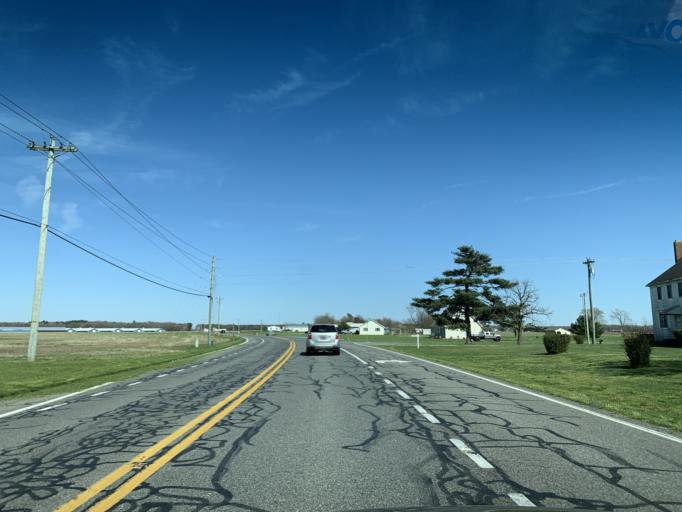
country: US
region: Delaware
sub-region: Kent County
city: Harrington
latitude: 38.8940
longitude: -75.6379
